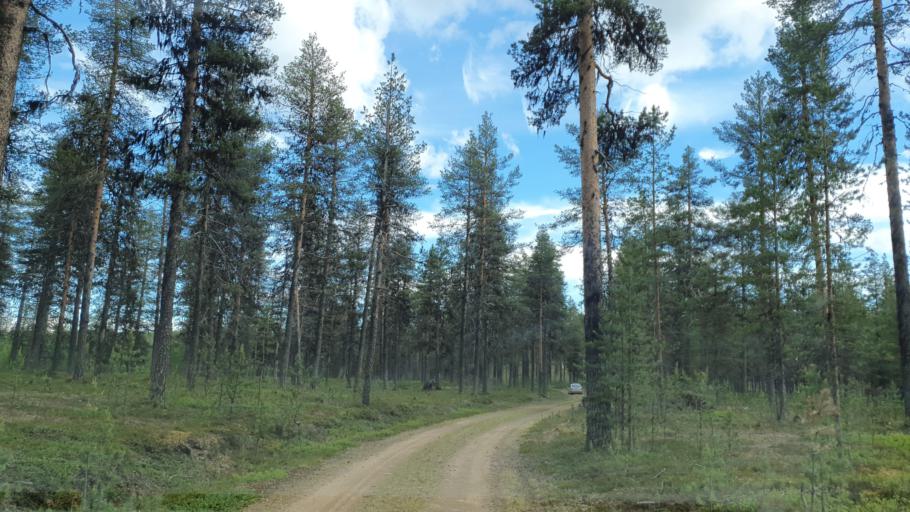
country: FI
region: Lapland
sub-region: Tunturi-Lappi
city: Kolari
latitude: 67.5379
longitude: 23.9148
